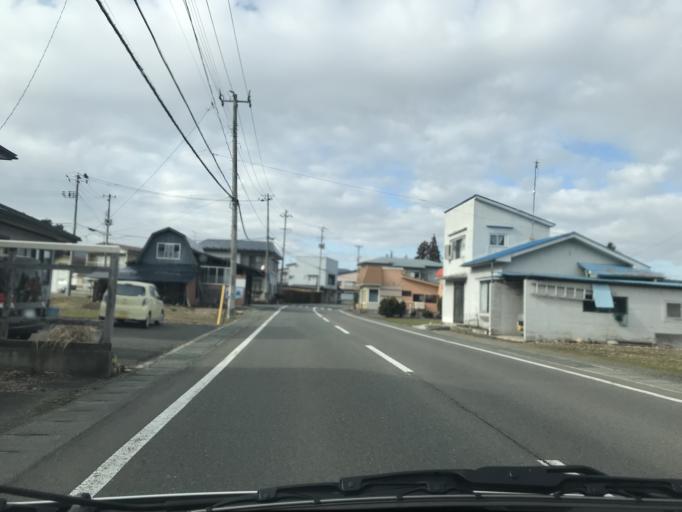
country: JP
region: Iwate
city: Hanamaki
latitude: 39.4237
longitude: 141.0850
